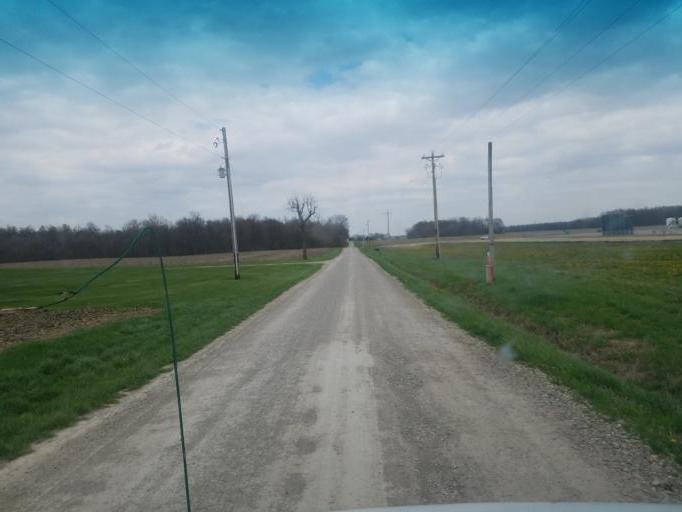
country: US
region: Ohio
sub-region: Crawford County
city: Bucyrus
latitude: 40.9793
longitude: -82.9720
